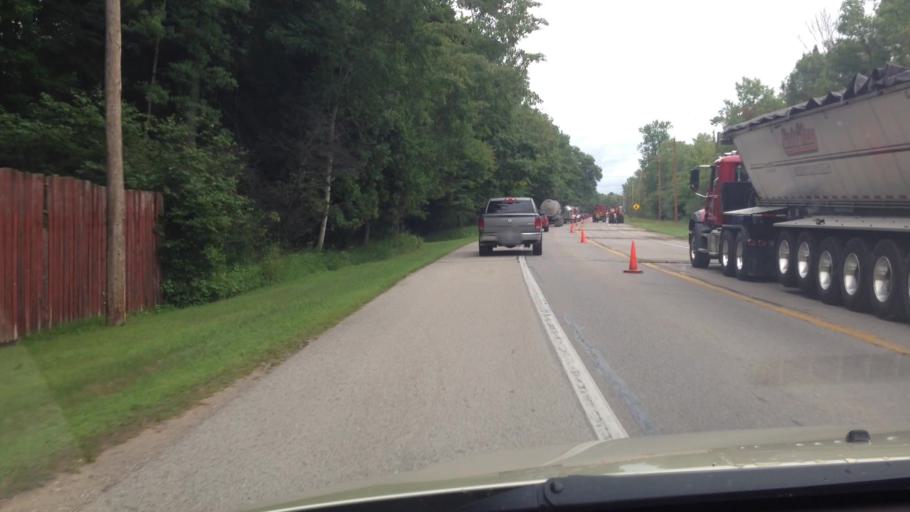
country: US
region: Michigan
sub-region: Delta County
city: Escanaba
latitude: 45.7072
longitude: -87.0991
